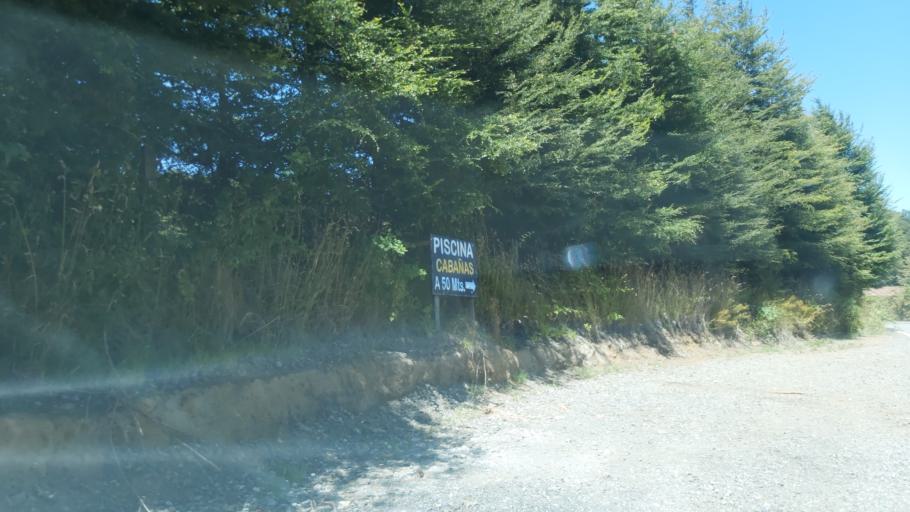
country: CL
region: Araucania
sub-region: Provincia de Cautin
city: Vilcun
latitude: -38.4652
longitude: -71.7630
